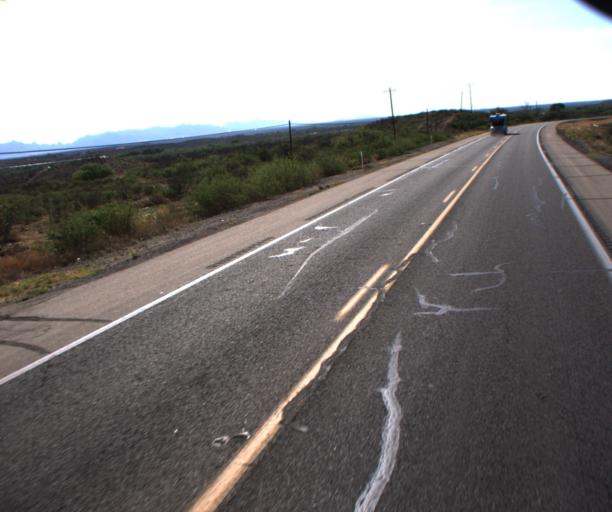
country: US
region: Arizona
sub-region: Cochise County
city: Saint David
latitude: 31.9200
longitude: -110.2670
